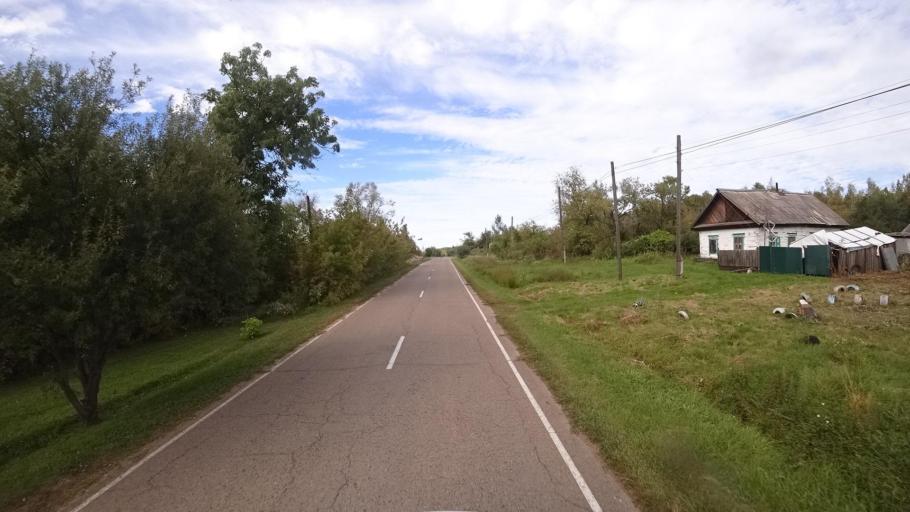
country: RU
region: Primorskiy
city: Dostoyevka
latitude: 44.3252
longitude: 133.4768
